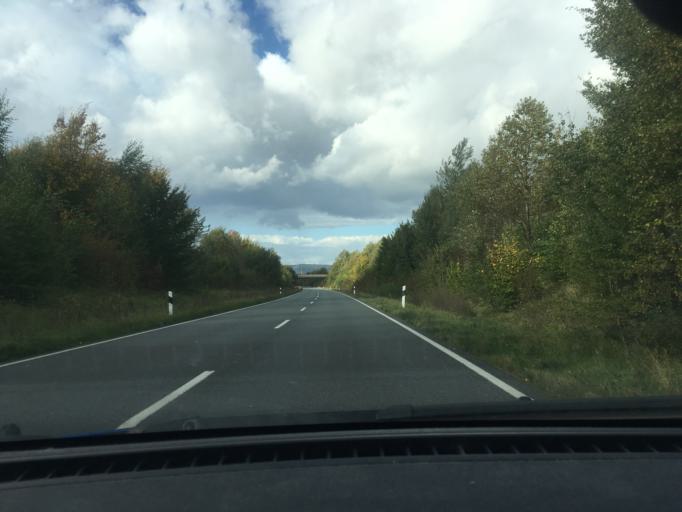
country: DE
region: Lower Saxony
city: Bevern
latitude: 51.8316
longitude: 9.4824
